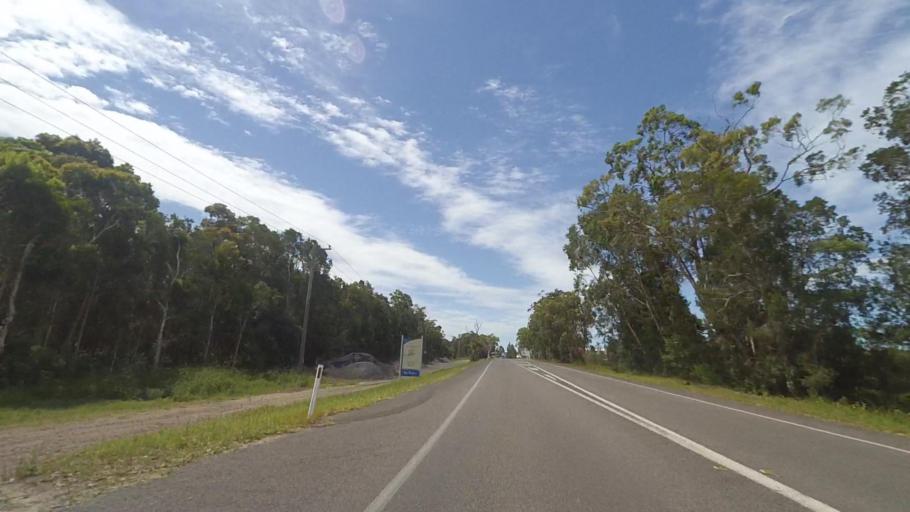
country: AU
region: New South Wales
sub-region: Port Stephens Shire
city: Anna Bay
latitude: -32.7555
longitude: 152.0682
